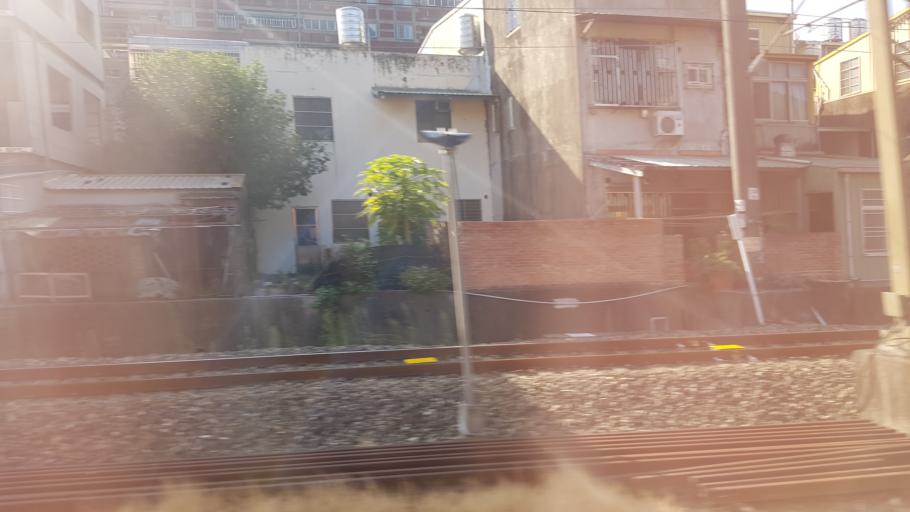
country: TW
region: Taiwan
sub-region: Miaoli
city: Miaoli
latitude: 24.4195
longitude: 120.7743
